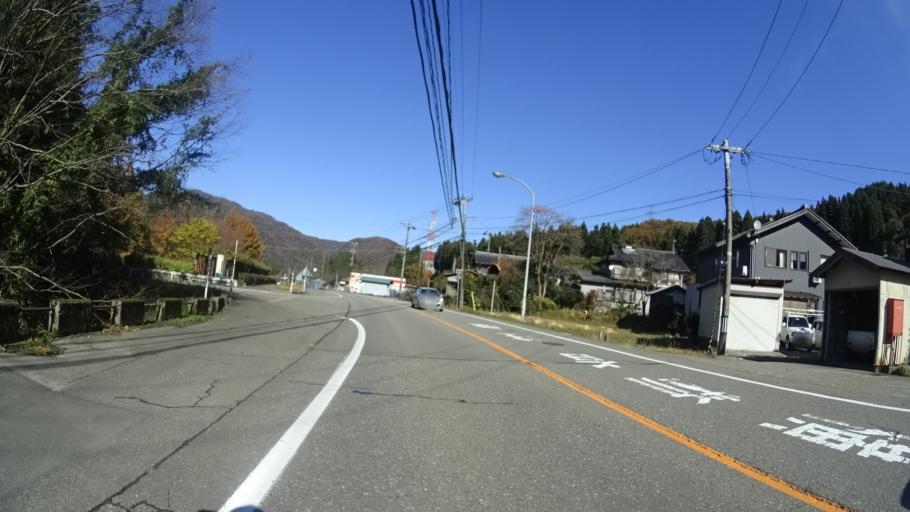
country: JP
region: Ishikawa
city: Tsurugi-asahimachi
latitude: 36.3788
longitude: 136.6155
